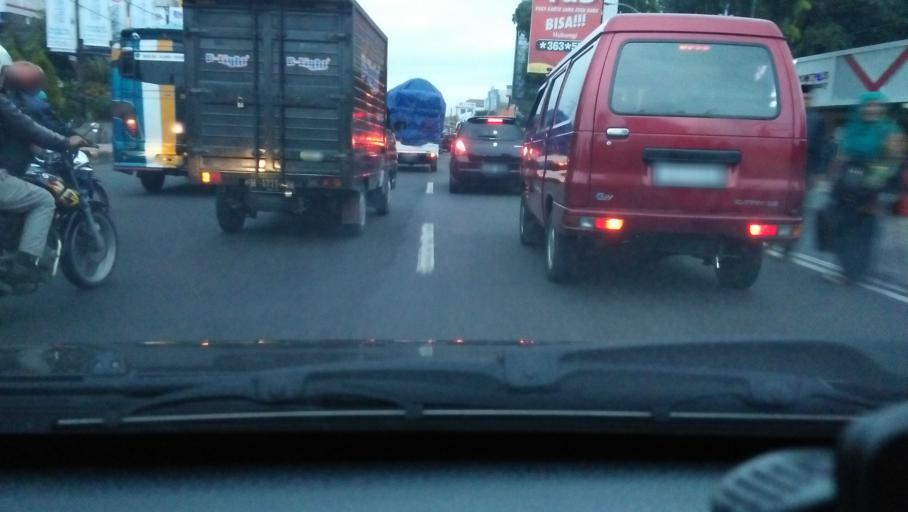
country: ID
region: Central Java
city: Mertoyudan
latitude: -7.5032
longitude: 110.2238
